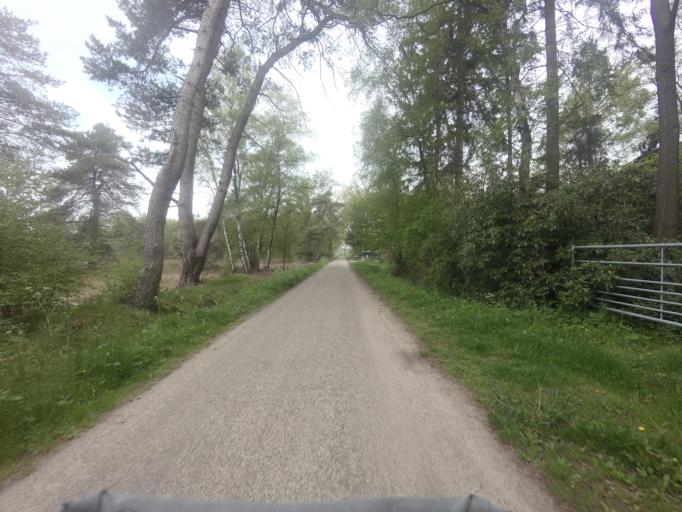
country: NL
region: Overijssel
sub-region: Gemeente Haaksbergen
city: Haaksbergen
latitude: 52.1850
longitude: 6.8141
